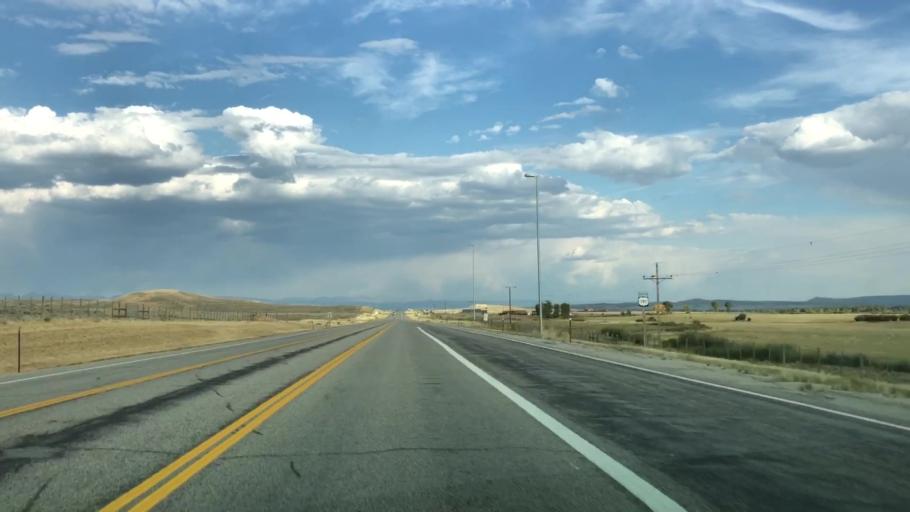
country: US
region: Wyoming
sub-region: Sublette County
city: Pinedale
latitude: 42.8894
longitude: -110.0663
